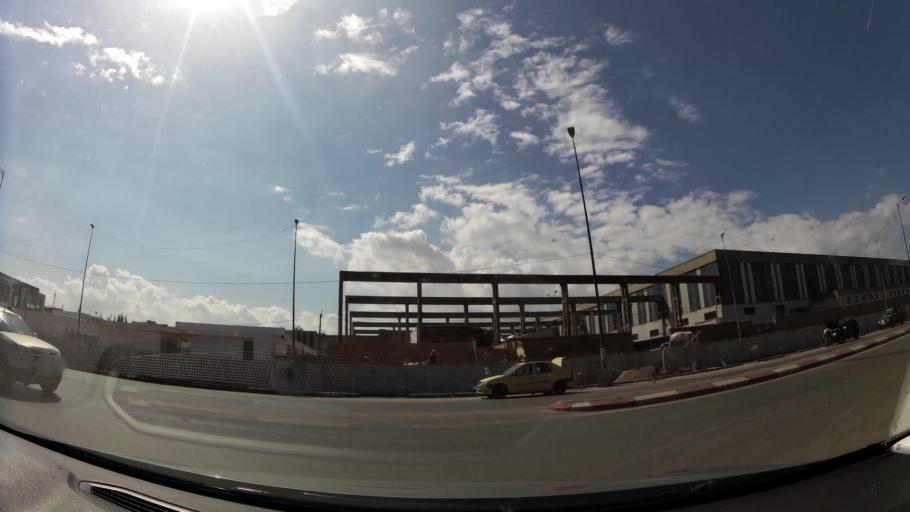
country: MA
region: Rabat-Sale-Zemmour-Zaer
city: Sale
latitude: 34.0635
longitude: -6.7981
